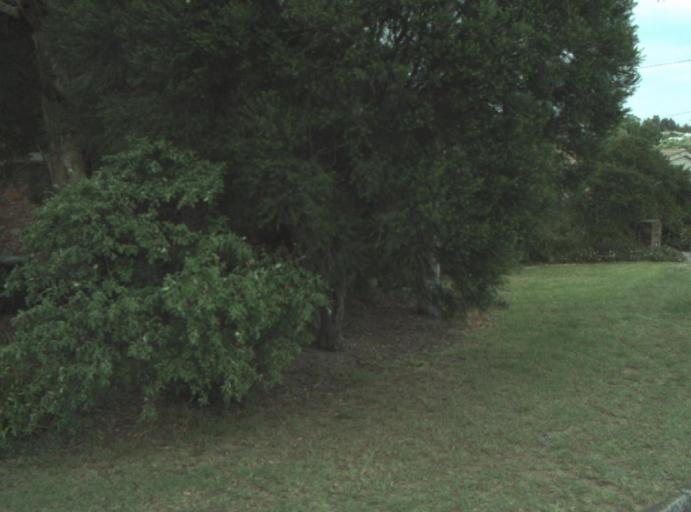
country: AU
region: Victoria
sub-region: Greater Geelong
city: Wandana Heights
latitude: -38.1773
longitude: 144.3057
